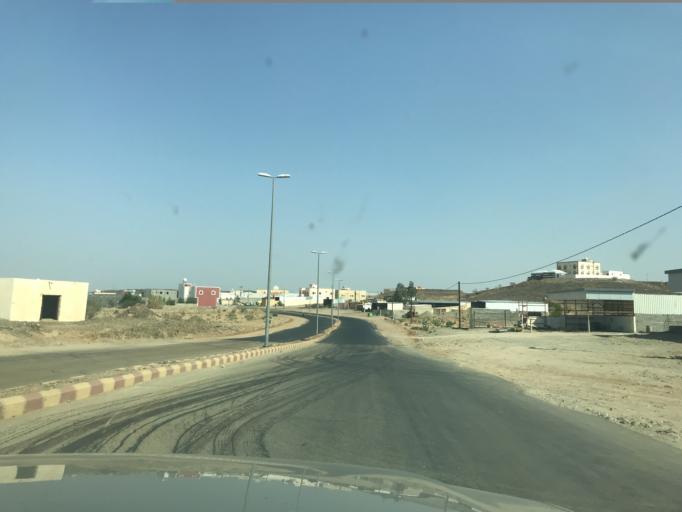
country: SA
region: Mintaqat al Bahah
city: Al Bahah
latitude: 20.4405
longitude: 41.9252
